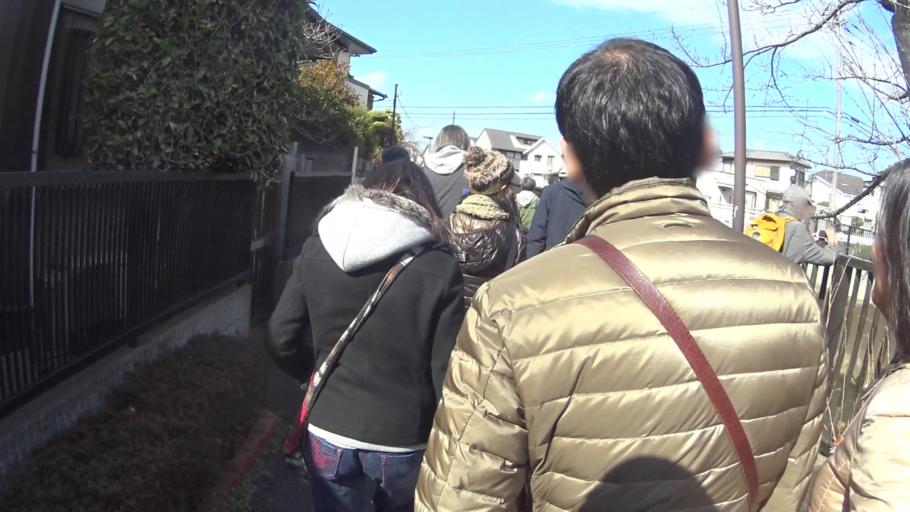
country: JP
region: Tokyo
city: Chofugaoka
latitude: 35.6487
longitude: 139.6020
